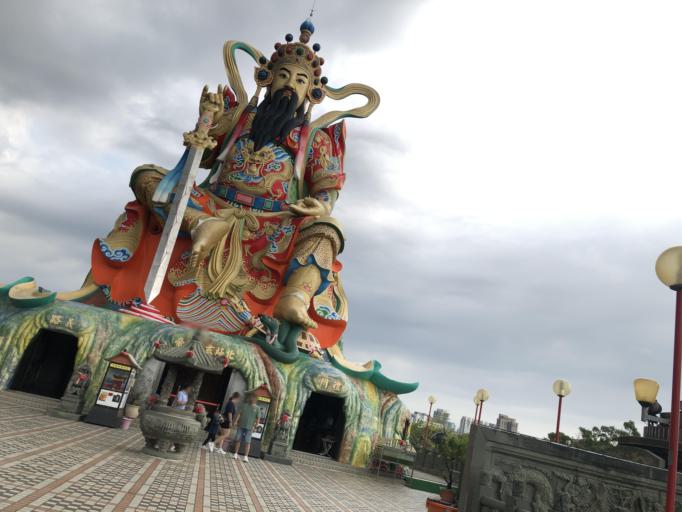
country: TW
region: Kaohsiung
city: Kaohsiung
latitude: 22.6845
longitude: 120.2962
